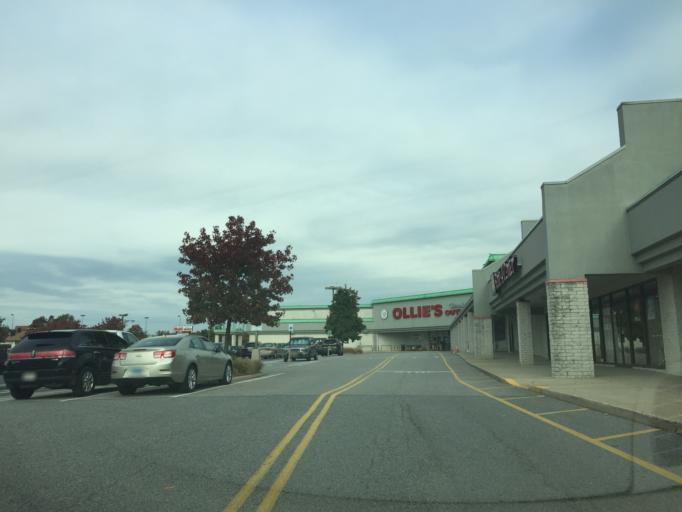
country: US
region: Maryland
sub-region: Baltimore County
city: Dundalk
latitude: 39.2761
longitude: -76.5029
